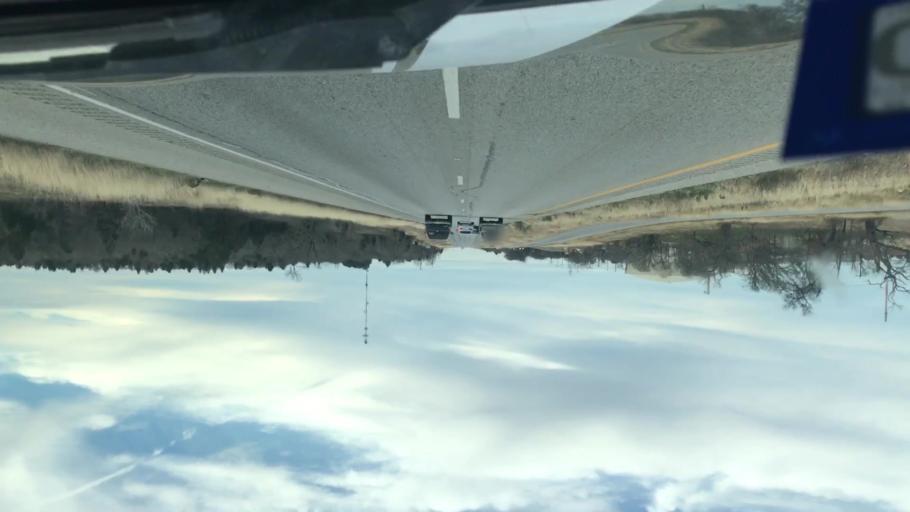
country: US
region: Texas
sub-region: Bastrop County
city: Elgin
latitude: 30.3300
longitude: -97.3449
